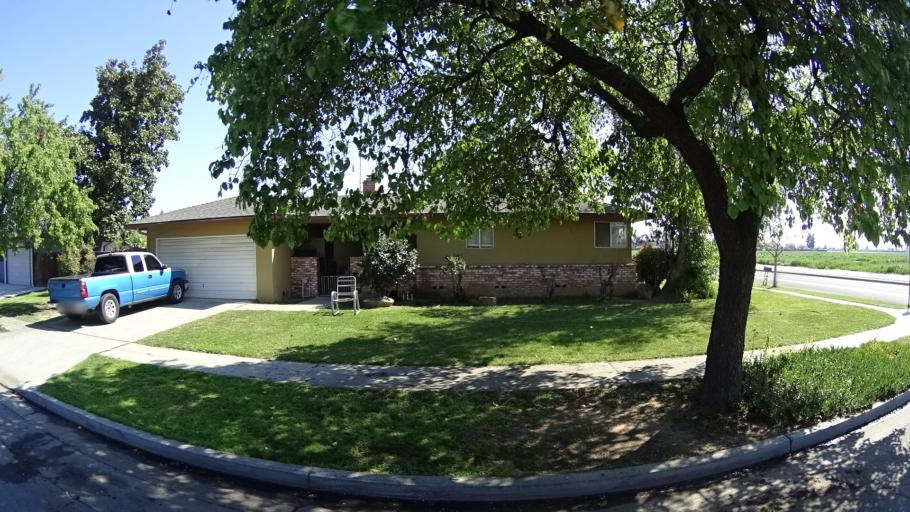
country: US
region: California
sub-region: Fresno County
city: Clovis
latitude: 36.8304
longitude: -119.7404
